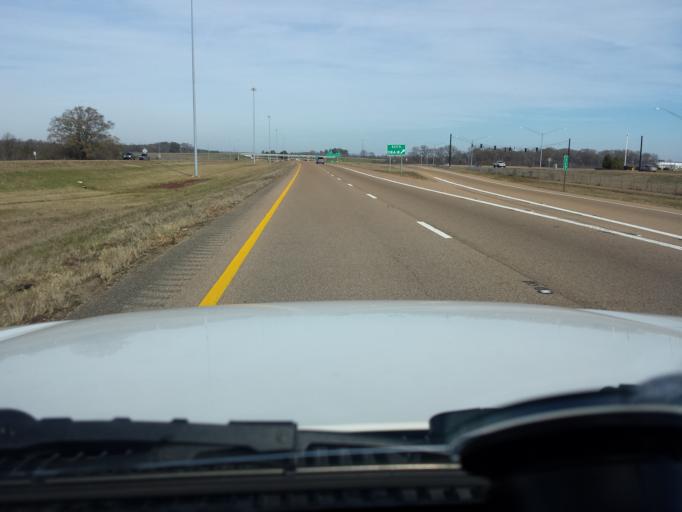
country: US
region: Mississippi
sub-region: Madison County
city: Canton
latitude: 32.5764
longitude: -90.0730
